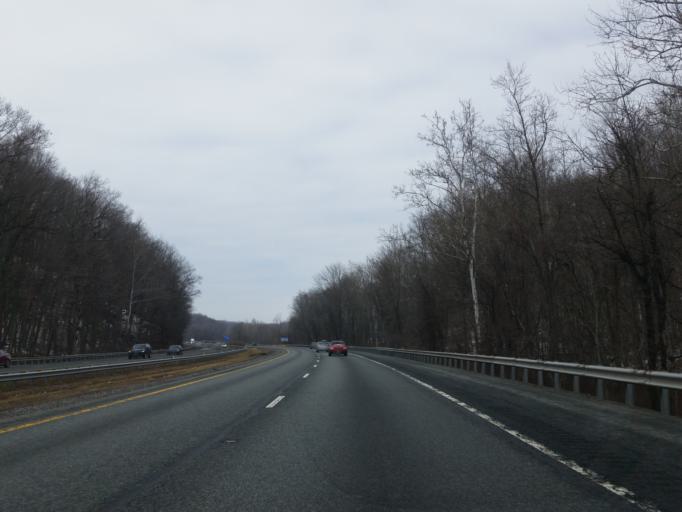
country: US
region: Maryland
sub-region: Baltimore County
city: Hunt Valley
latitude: 39.5643
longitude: -76.6661
